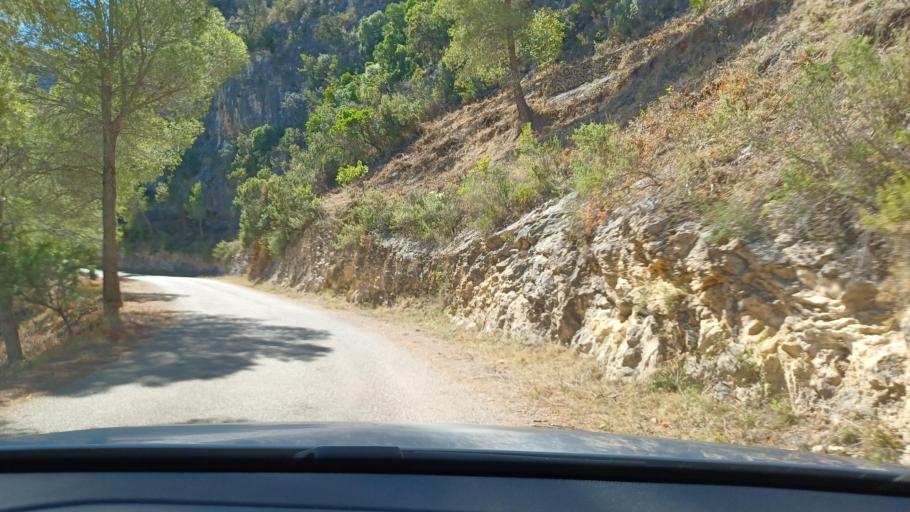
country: ES
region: Catalonia
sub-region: Provincia de Tarragona
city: Benifallet
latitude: 40.9517
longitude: 0.5103
